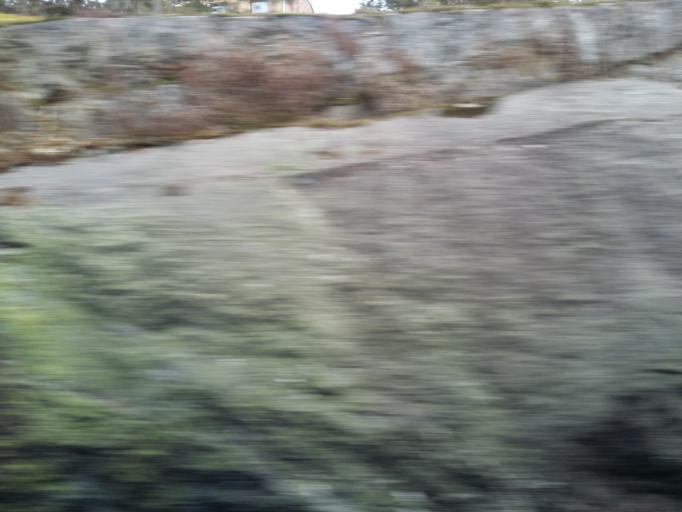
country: NO
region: Akershus
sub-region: Oppegard
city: Kolbotn
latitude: 59.8799
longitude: 10.8415
